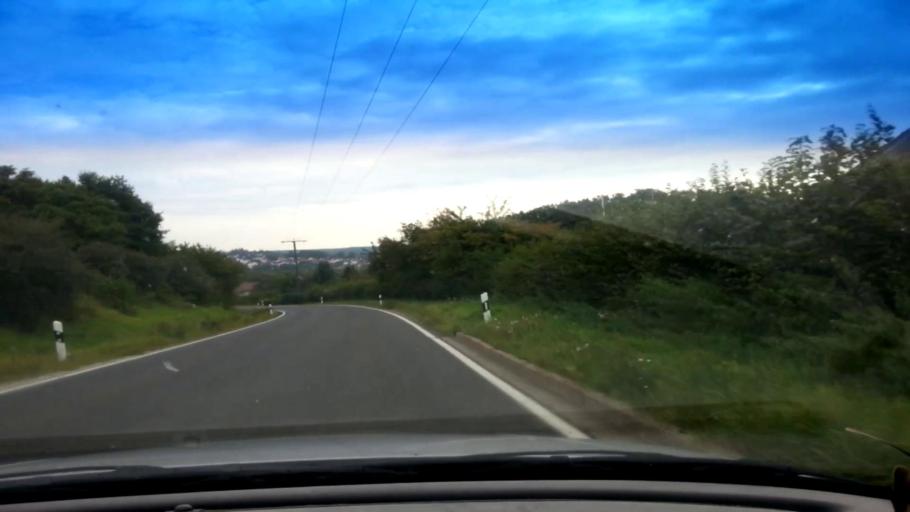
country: DE
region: Bavaria
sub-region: Upper Franconia
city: Memmelsdorf
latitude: 49.9450
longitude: 10.9566
